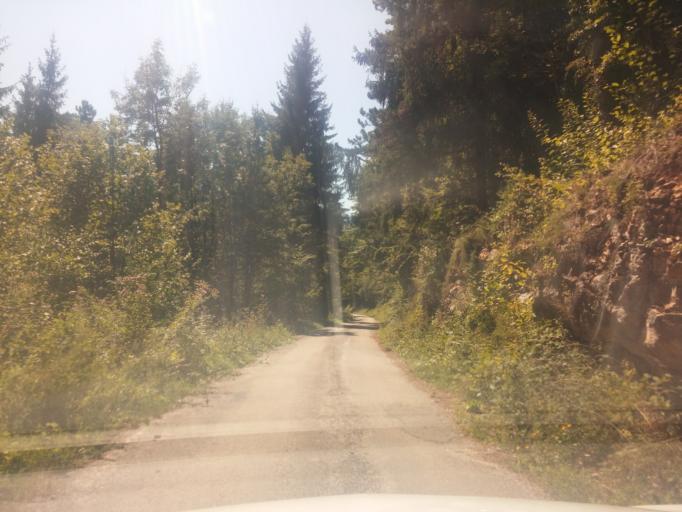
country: FR
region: Franche-Comte
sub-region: Departement du Jura
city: Saint-Lupicin
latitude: 46.4120
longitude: 5.7865
